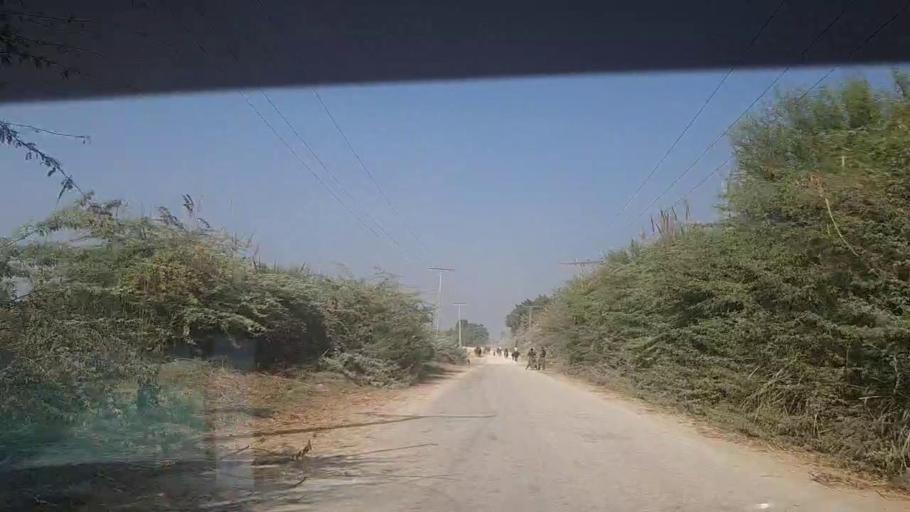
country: PK
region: Sindh
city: Kot Diji
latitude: 27.3570
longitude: 68.7105
